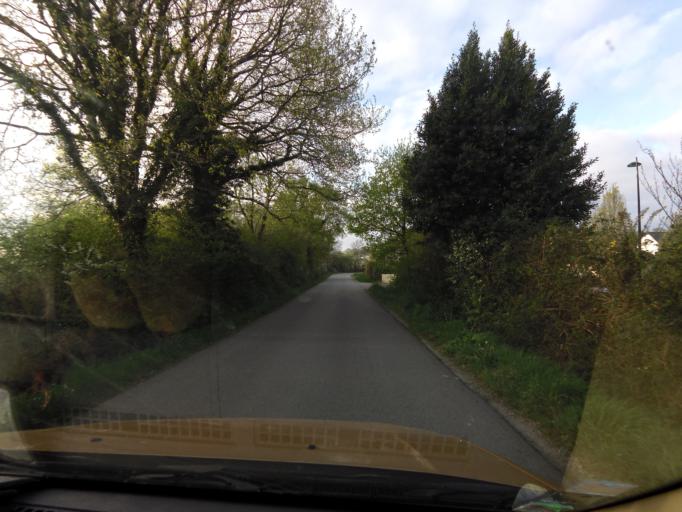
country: FR
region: Brittany
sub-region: Departement du Morbihan
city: Arradon
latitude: 47.6322
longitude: -2.8132
